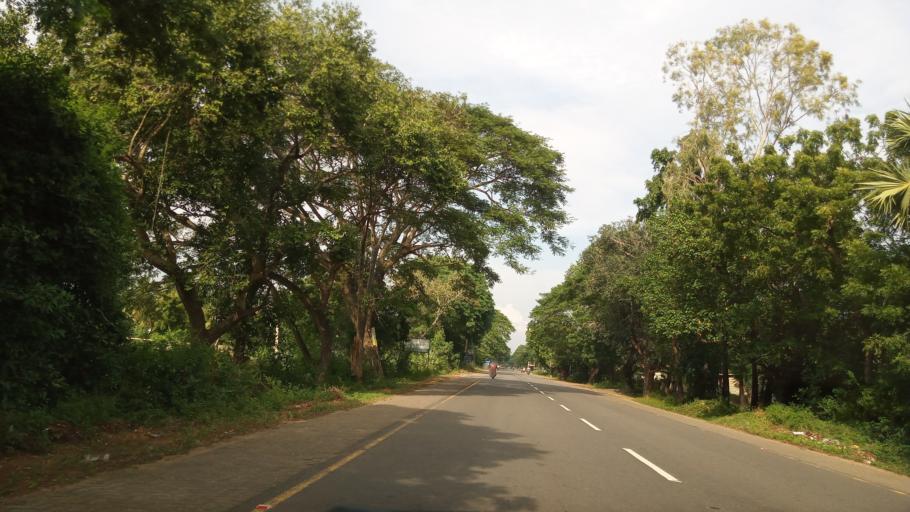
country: IN
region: Tamil Nadu
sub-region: Villupuram
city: Auroville
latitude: 12.0623
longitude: 79.8770
